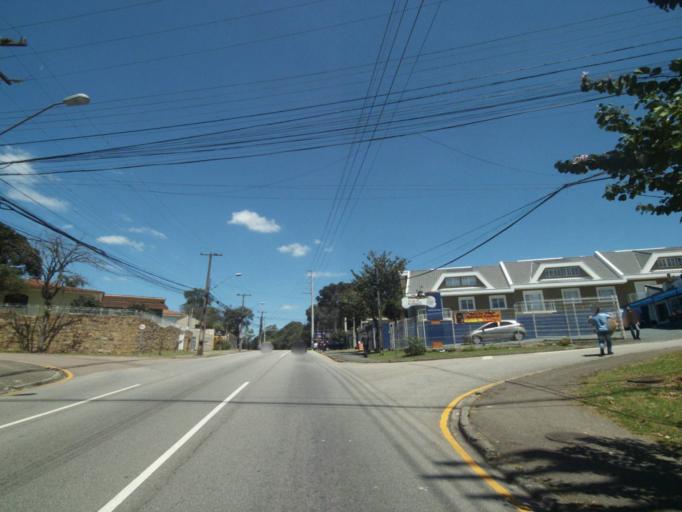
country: BR
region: Parana
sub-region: Curitiba
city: Curitiba
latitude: -25.3955
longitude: -49.2732
